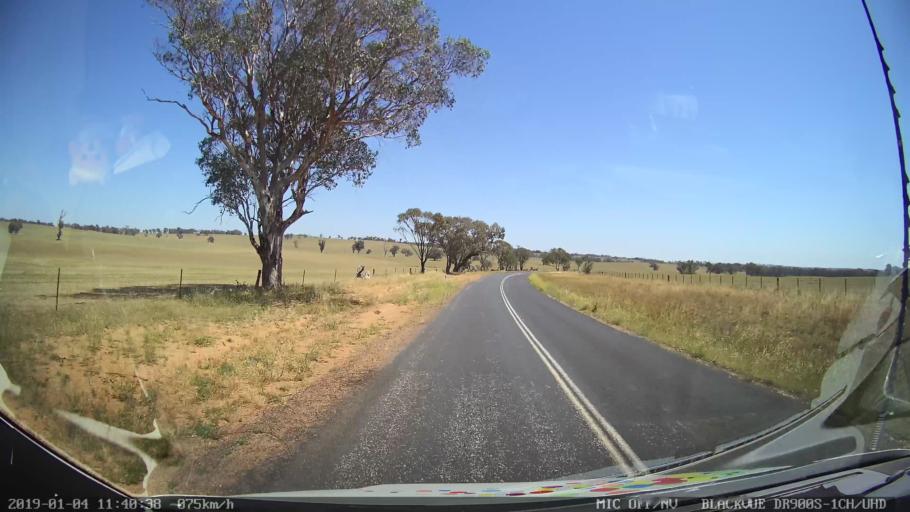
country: AU
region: New South Wales
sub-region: Cabonne
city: Molong
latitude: -33.0032
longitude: 148.7863
